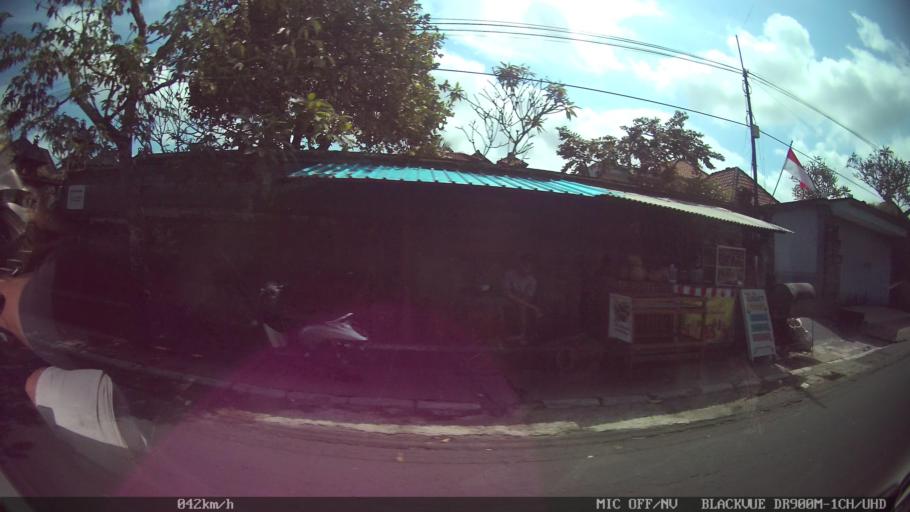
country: ID
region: Bali
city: Banjar Kelodan
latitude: -8.5307
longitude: 115.3287
